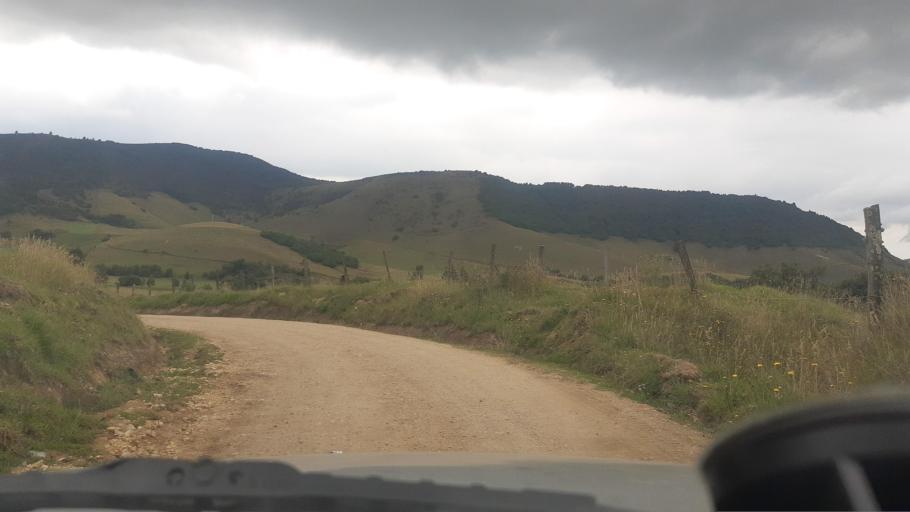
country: CO
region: Cundinamarca
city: Suesca
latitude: 5.1531
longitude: -73.7939
